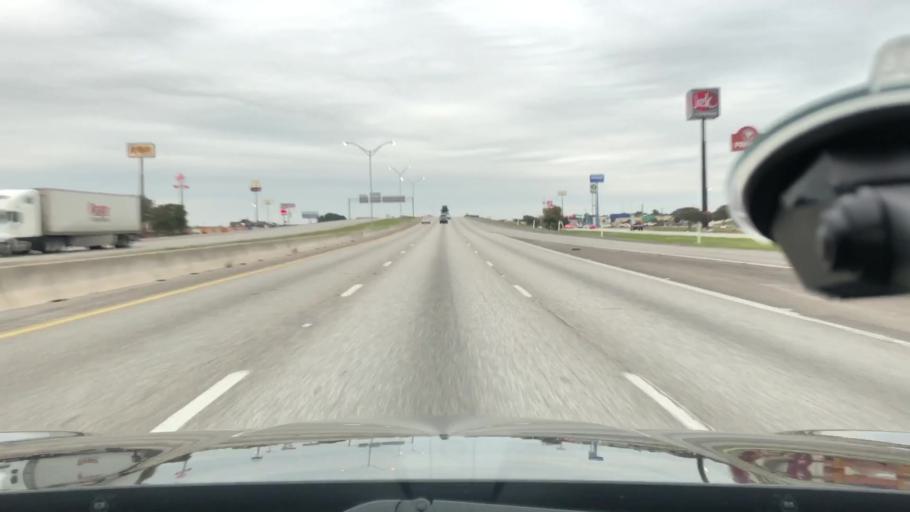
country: US
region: Texas
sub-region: McLennan County
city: Bellmead
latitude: 31.6010
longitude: -97.1079
